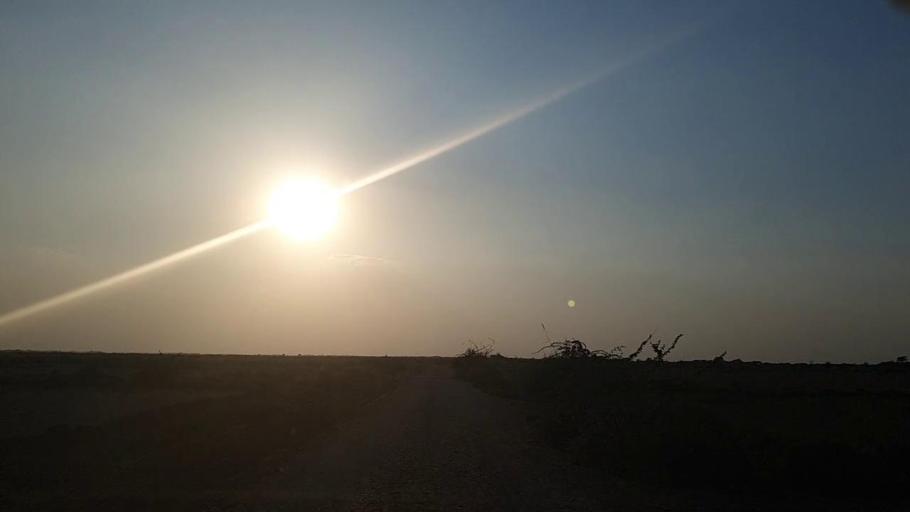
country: PK
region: Sindh
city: Jati
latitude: 24.4847
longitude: 68.4148
